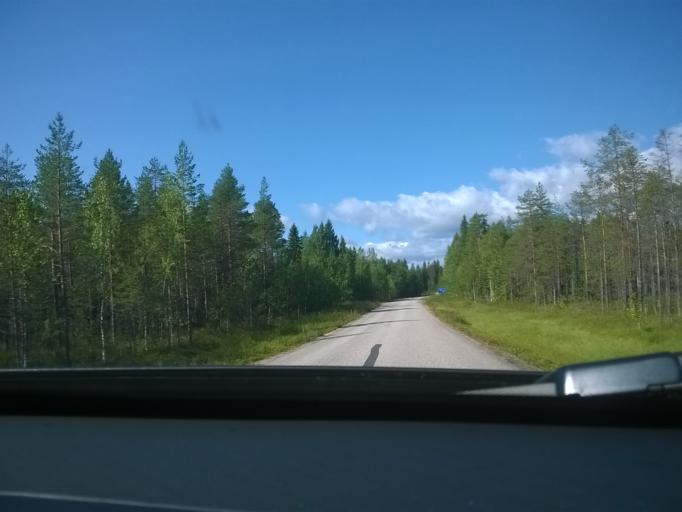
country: FI
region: Kainuu
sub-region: Kehys-Kainuu
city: Kuhmo
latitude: 64.4604
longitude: 29.6090
